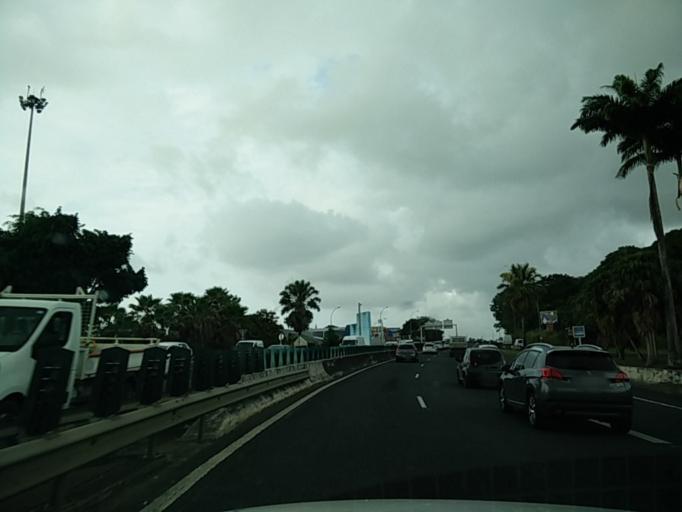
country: GP
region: Guadeloupe
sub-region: Guadeloupe
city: Baie-Mahault
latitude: 16.2516
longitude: -61.5881
